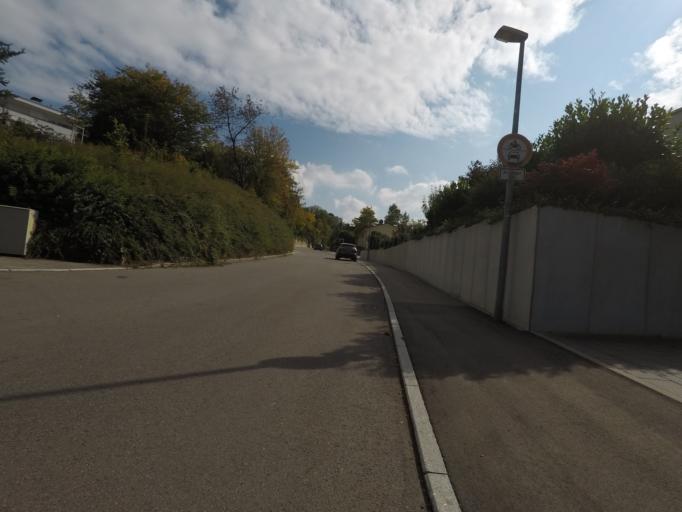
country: DE
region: Baden-Wuerttemberg
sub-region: Tuebingen Region
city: Reutlingen
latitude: 48.4982
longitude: 9.2255
